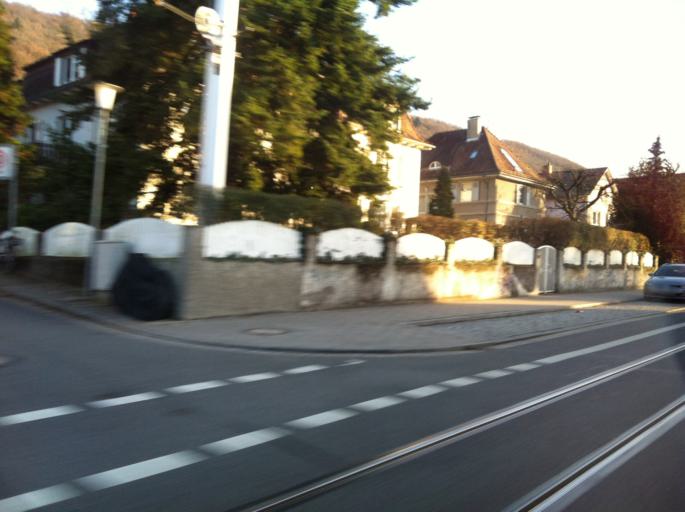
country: DE
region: Baden-Wuerttemberg
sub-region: Karlsruhe Region
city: Heidelberg
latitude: 49.3940
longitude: 8.6900
